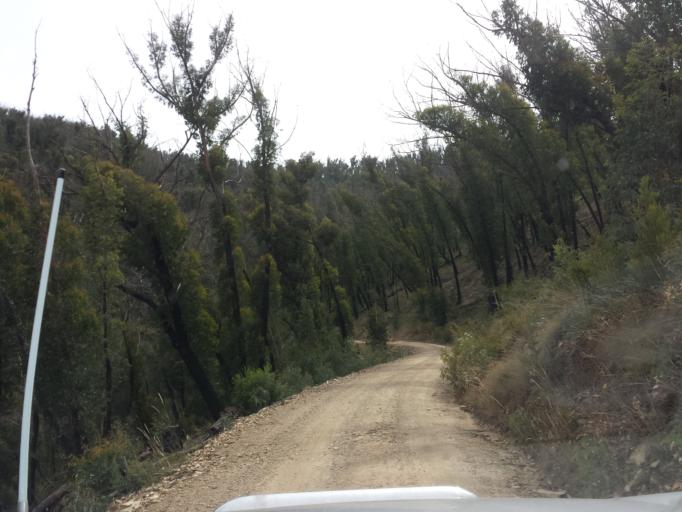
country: AU
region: Victoria
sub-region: Wellington
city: Heyfield
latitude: -37.7453
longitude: 146.4081
